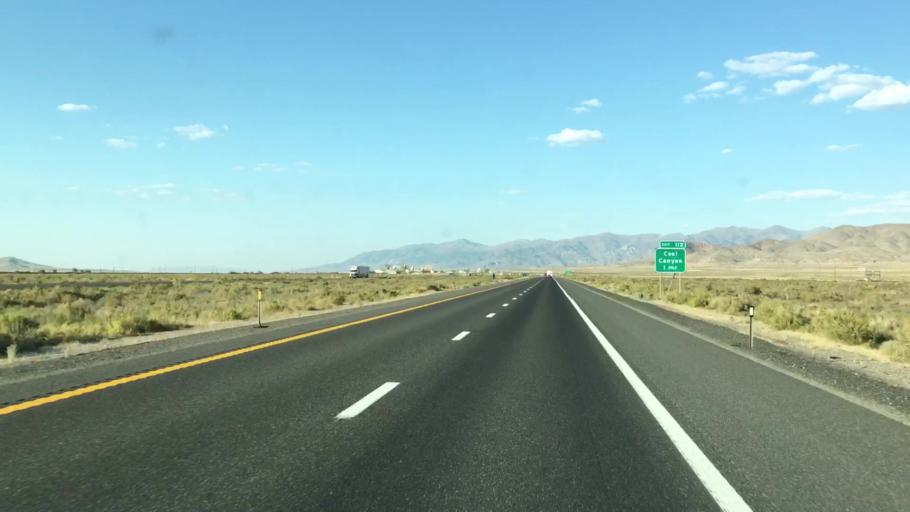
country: US
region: Nevada
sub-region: Pershing County
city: Lovelock
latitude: 40.2262
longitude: -118.4070
